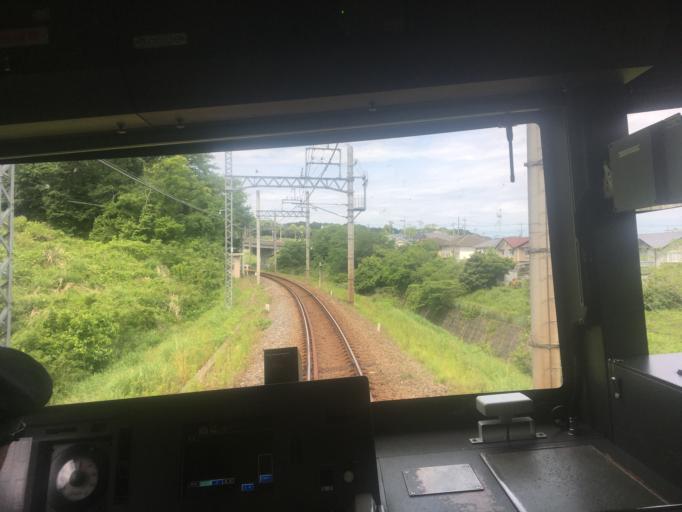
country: JP
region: Saitama
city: Ogawa
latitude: 36.0572
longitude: 139.2983
